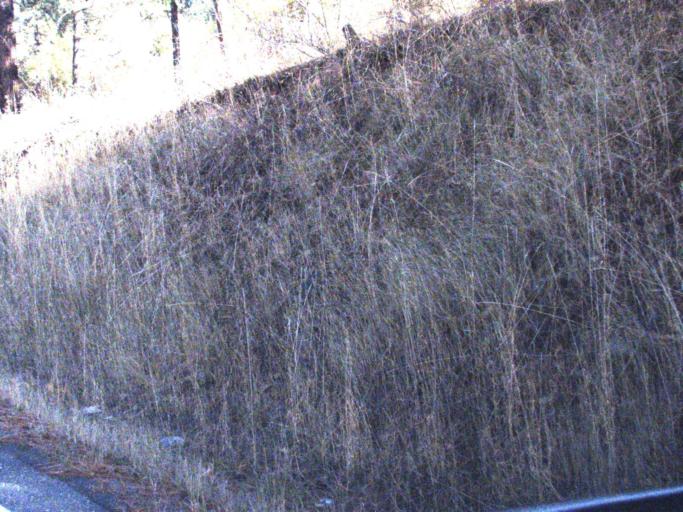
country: US
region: Washington
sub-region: Stevens County
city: Kettle Falls
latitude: 48.6656
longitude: -118.0528
